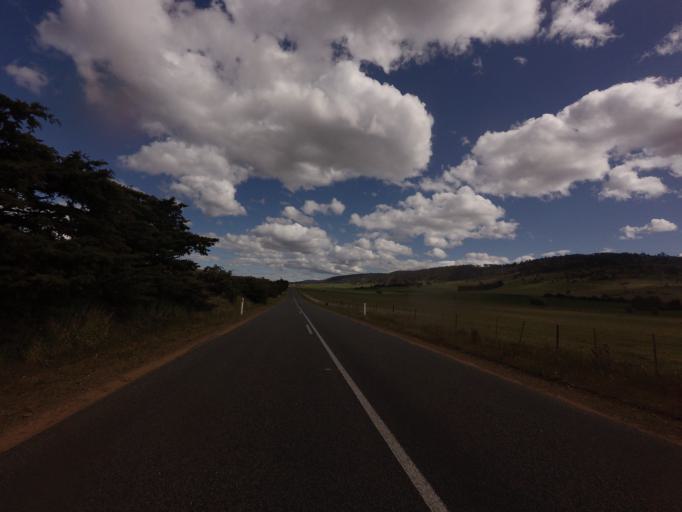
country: AU
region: Tasmania
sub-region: Brighton
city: Bridgewater
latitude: -42.4054
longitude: 147.3104
